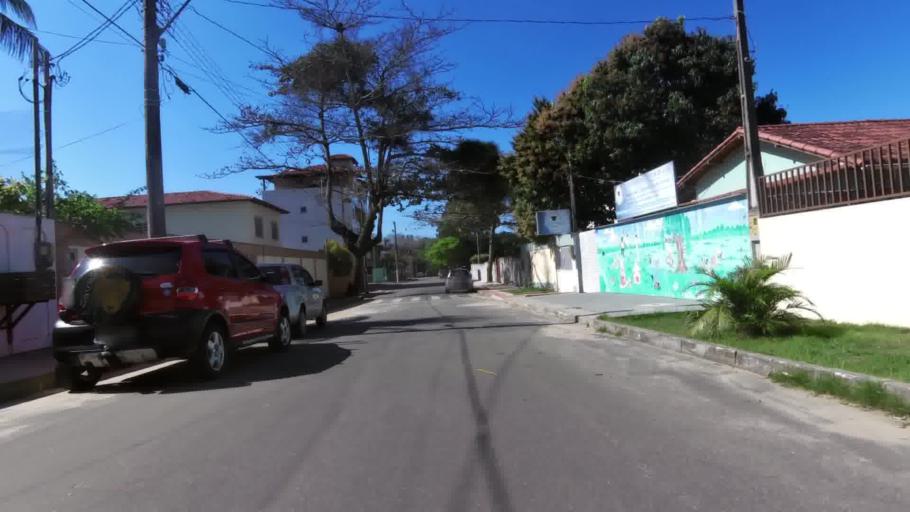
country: BR
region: Espirito Santo
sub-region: Guarapari
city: Guarapari
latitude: -20.7366
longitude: -40.5425
